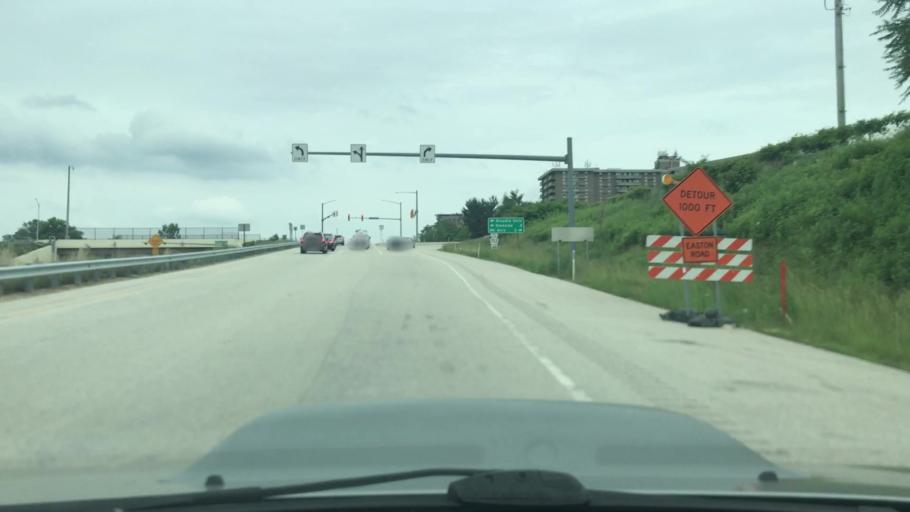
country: US
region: Pennsylvania
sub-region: Montgomery County
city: Wyncote
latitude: 40.0881
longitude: -75.1660
